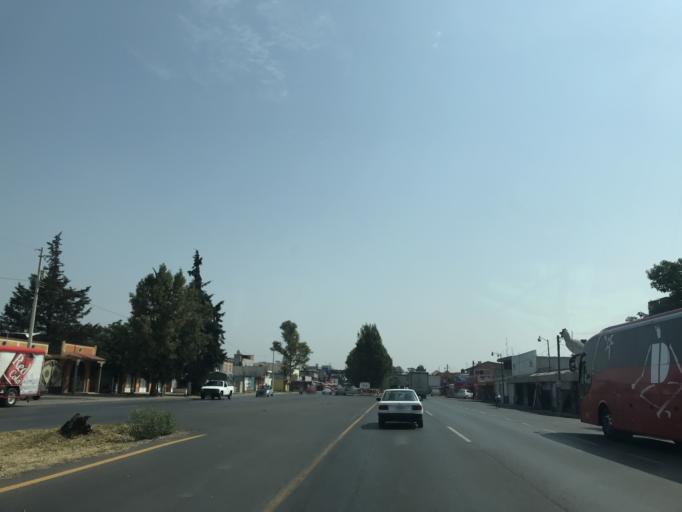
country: MX
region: Tlaxcala
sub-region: Apetatitlan de Antonio Carvajal
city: Tlatempan
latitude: 19.3302
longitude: -98.1992
